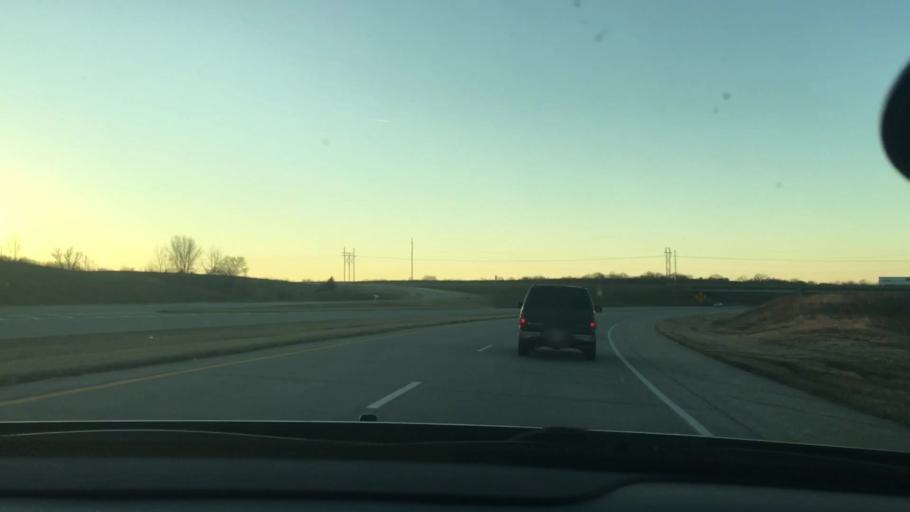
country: US
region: Oklahoma
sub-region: Pontotoc County
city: Ada
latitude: 34.7927
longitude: -96.6938
